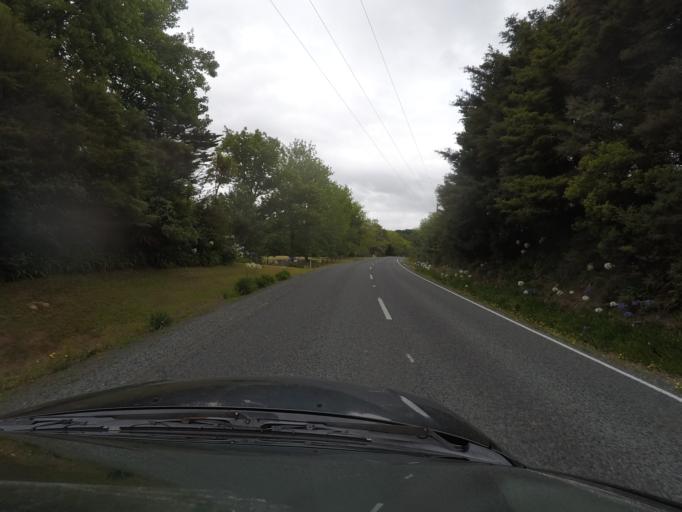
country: NZ
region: Auckland
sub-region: Auckland
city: Wellsford
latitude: -36.2805
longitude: 174.5936
